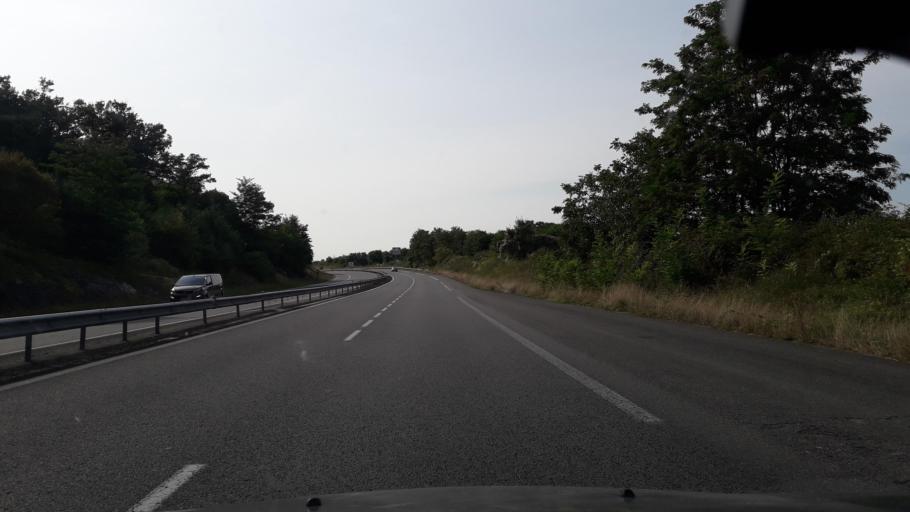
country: FR
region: Poitou-Charentes
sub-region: Departement de la Charente
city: Jarnac
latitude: 45.6676
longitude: -0.1821
